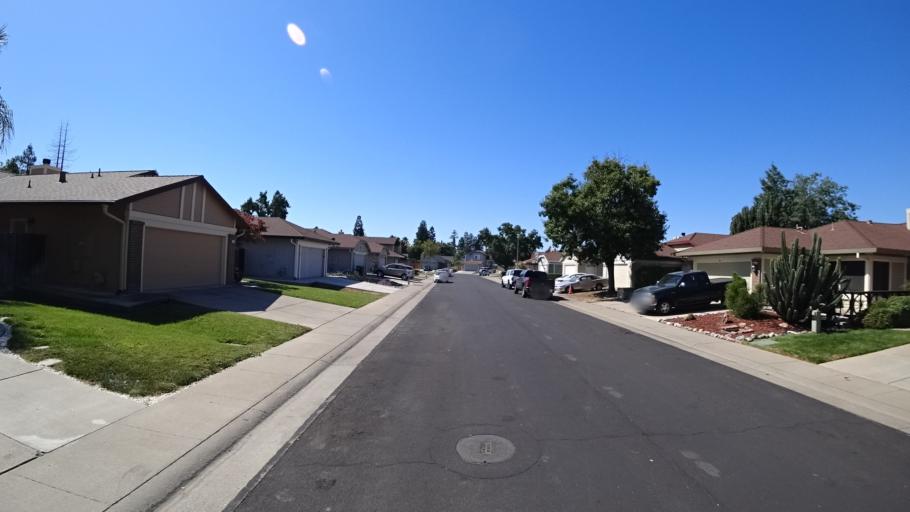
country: US
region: California
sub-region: Sacramento County
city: Laguna
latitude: 38.4331
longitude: -121.4420
